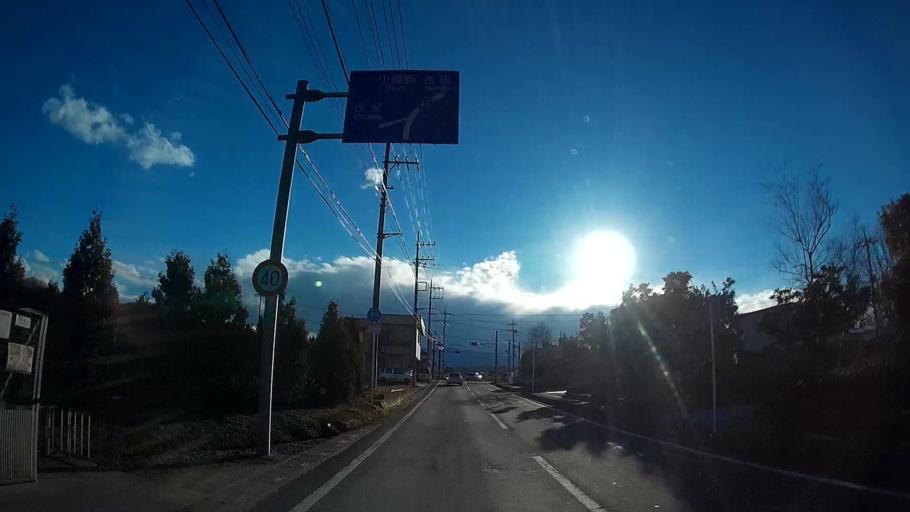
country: JP
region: Saitama
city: Chichibu
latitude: 36.0624
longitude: 139.0841
